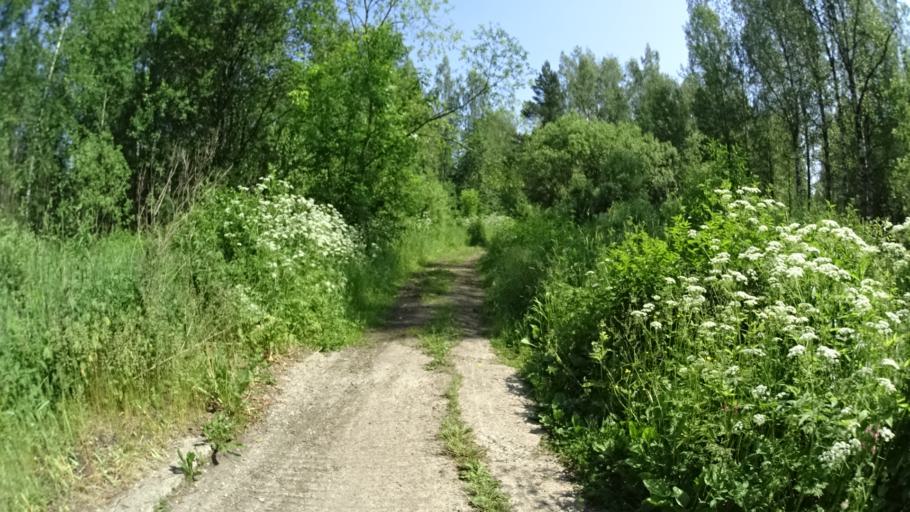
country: RU
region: Moskovskaya
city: Lesnoy
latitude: 56.0804
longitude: 37.9504
